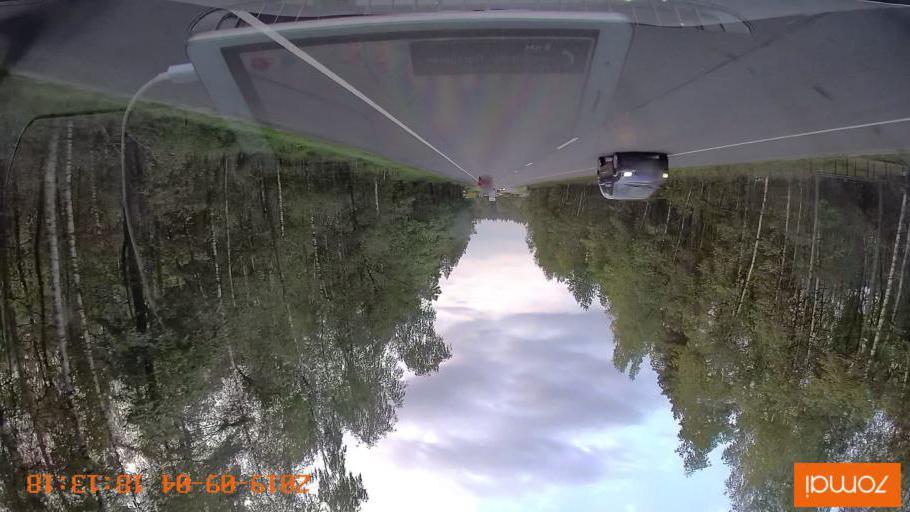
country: RU
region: Moskovskaya
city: Lopatinskiy
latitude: 55.3618
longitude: 38.7349
